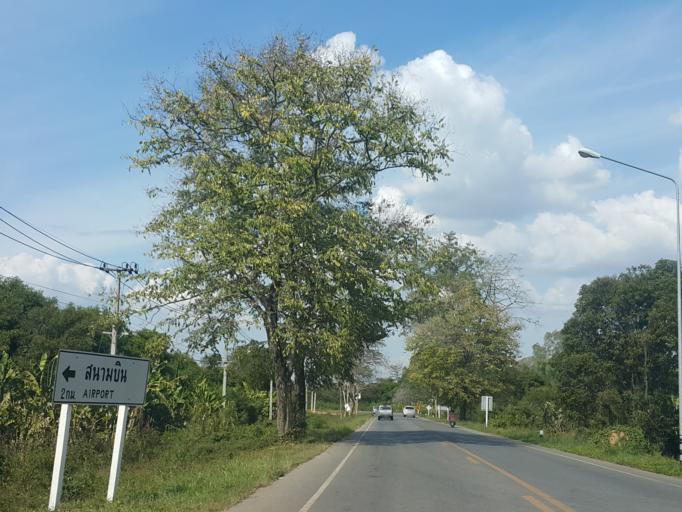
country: TH
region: Sukhothai
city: Sawankhalok
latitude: 17.2452
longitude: 99.8474
